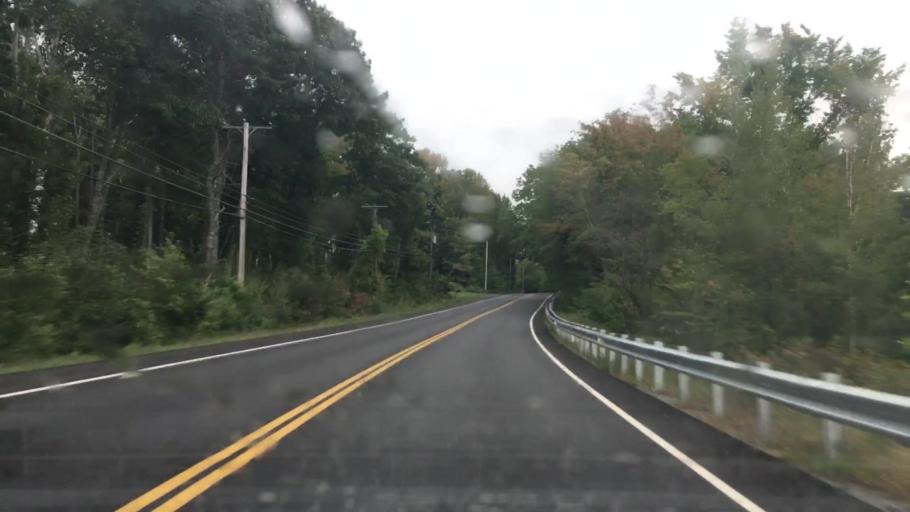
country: US
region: Maine
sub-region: Penobscot County
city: Orrington
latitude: 44.6816
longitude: -68.8088
